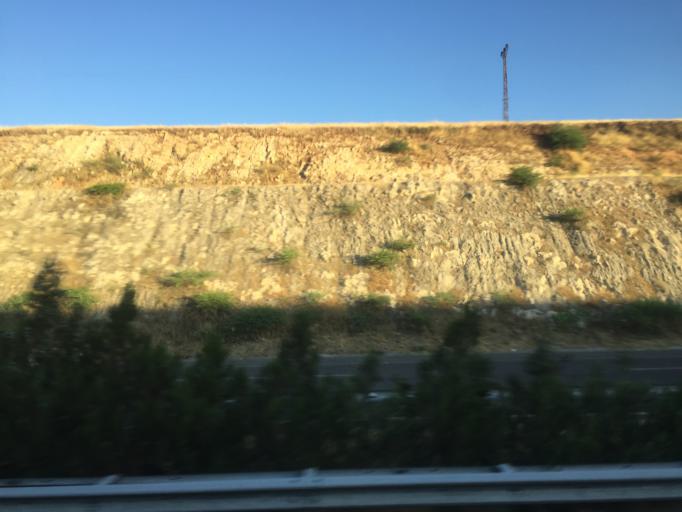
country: TR
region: Sanliurfa
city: Bogurtlen
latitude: 37.1019
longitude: 38.2056
